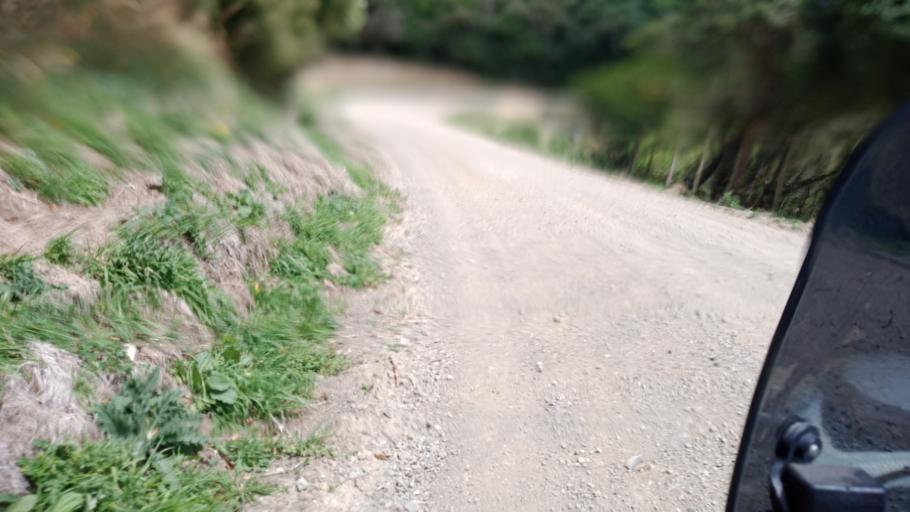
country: NZ
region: Gisborne
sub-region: Gisborne District
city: Gisborne
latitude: -38.4621
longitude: 177.5377
